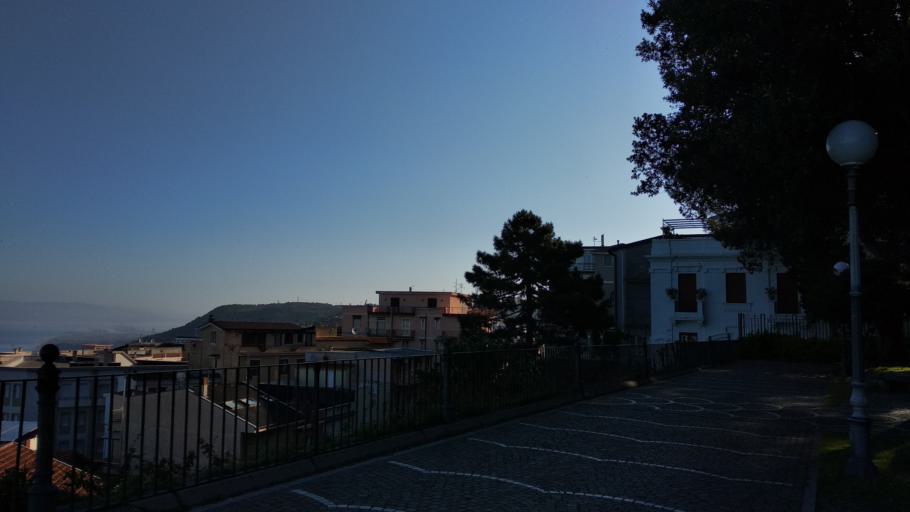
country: IT
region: Calabria
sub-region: Provincia di Reggio Calabria
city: Seminara
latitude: 38.3574
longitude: 15.8441
